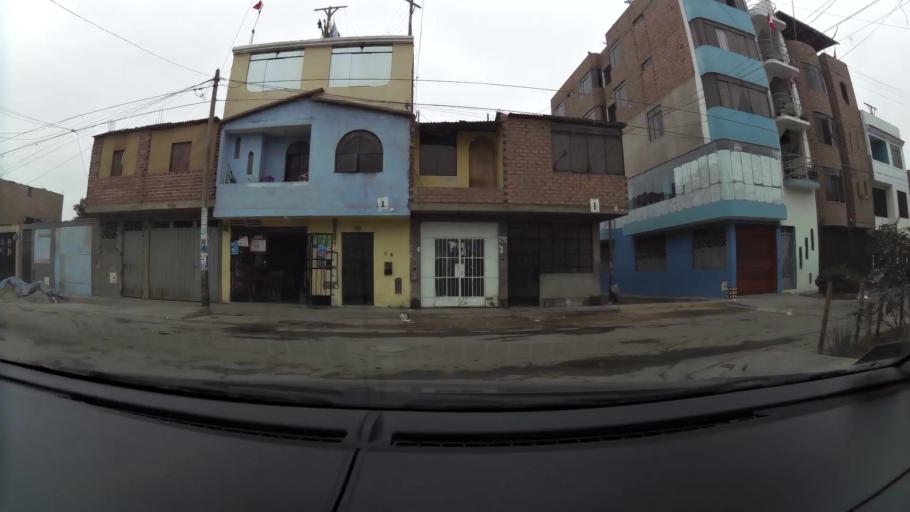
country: PE
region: Lima
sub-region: Lima
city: Independencia
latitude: -11.9665
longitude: -77.0776
